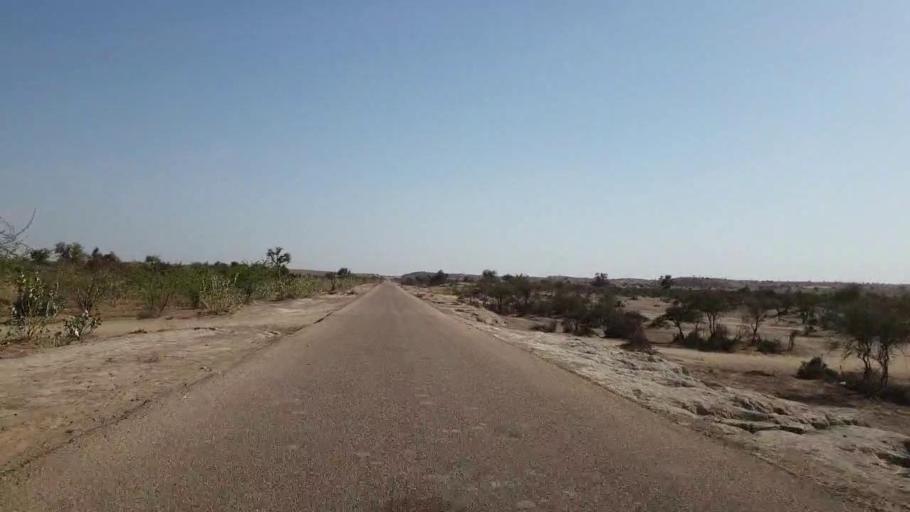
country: PK
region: Sindh
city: Nabisar
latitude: 25.0969
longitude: 70.0388
